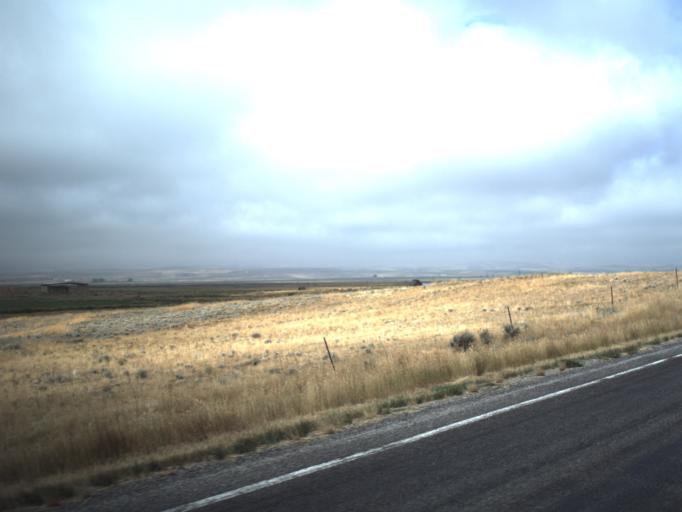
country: US
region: Utah
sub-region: Rich County
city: Randolph
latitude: 41.4795
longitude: -111.1147
